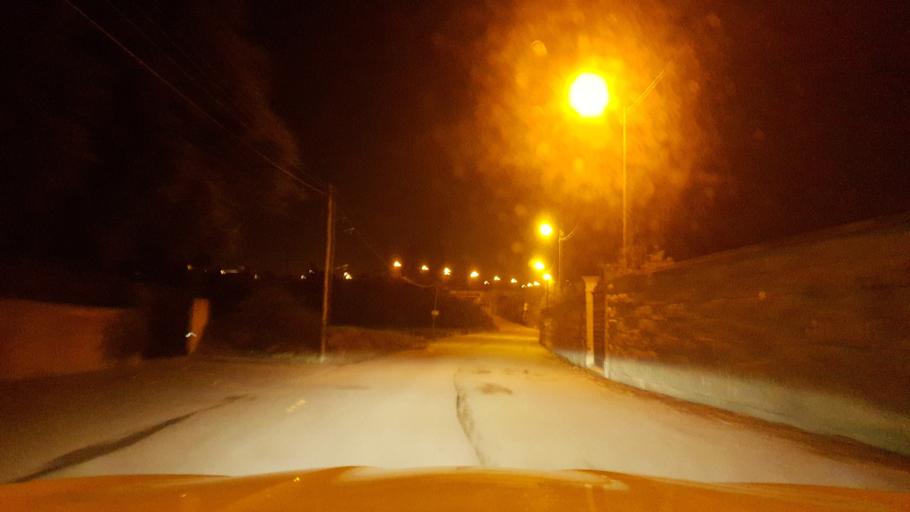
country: PT
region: Porto
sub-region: Matosinhos
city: Guifoes
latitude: 41.2136
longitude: -8.6430
